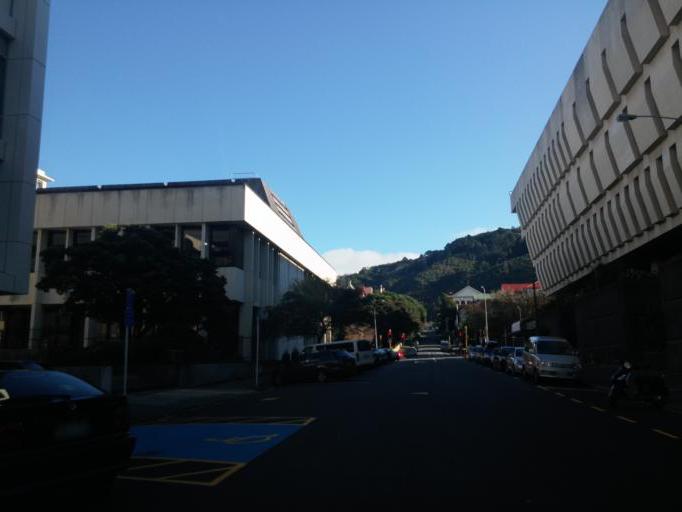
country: NZ
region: Wellington
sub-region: Wellington City
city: Wellington
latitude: -41.2770
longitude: 174.7789
